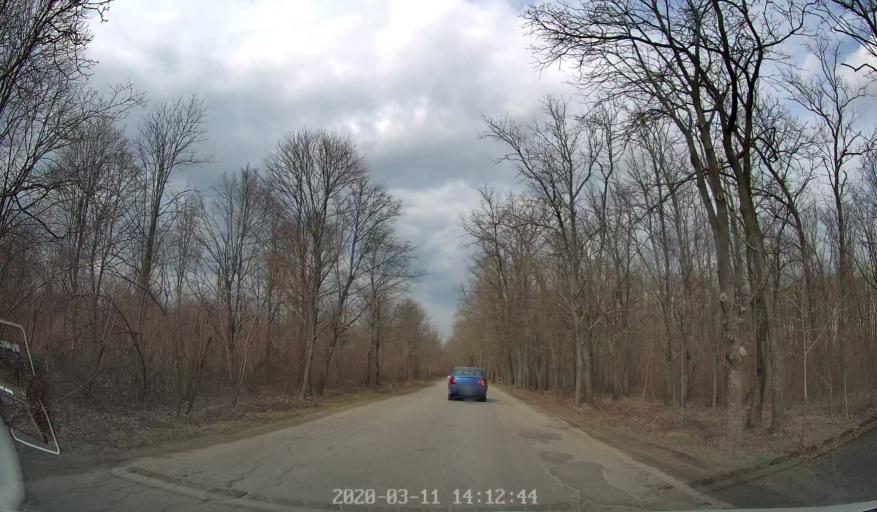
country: MD
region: Chisinau
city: Stauceni
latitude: 47.0547
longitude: 28.8839
